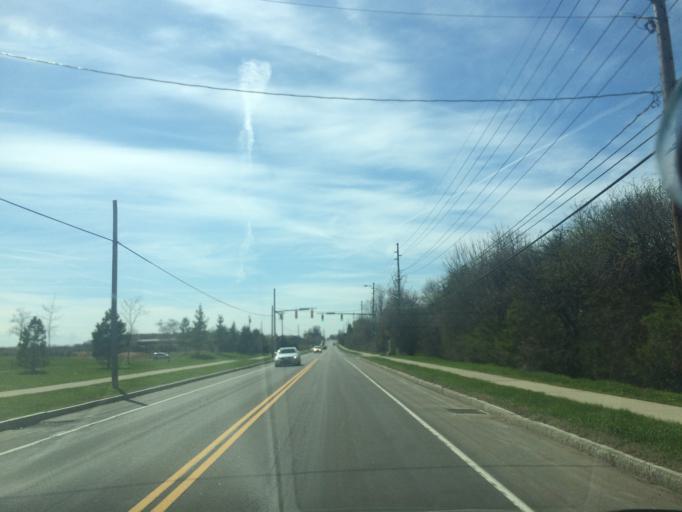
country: US
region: New York
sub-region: Monroe County
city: Brighton
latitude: 43.1156
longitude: -77.5842
